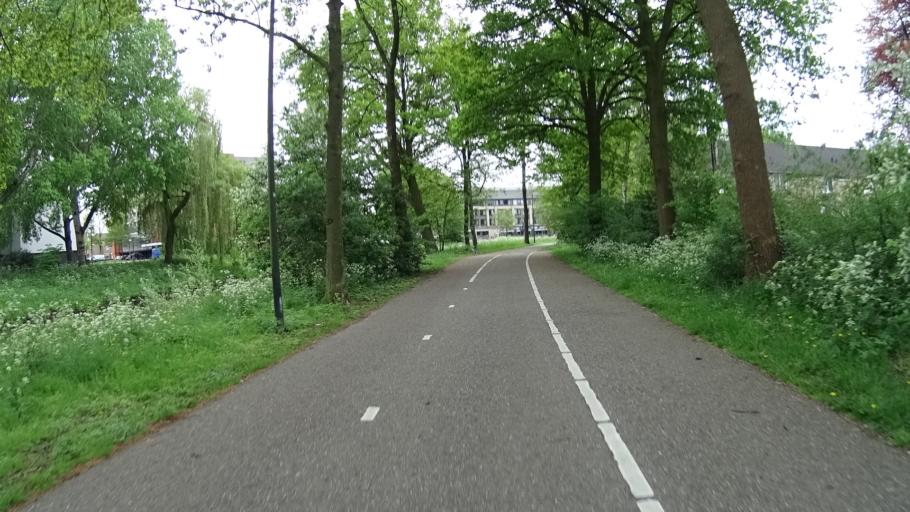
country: NL
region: North Brabant
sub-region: Gemeente Veghel
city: Veghel
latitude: 51.6111
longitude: 5.5451
